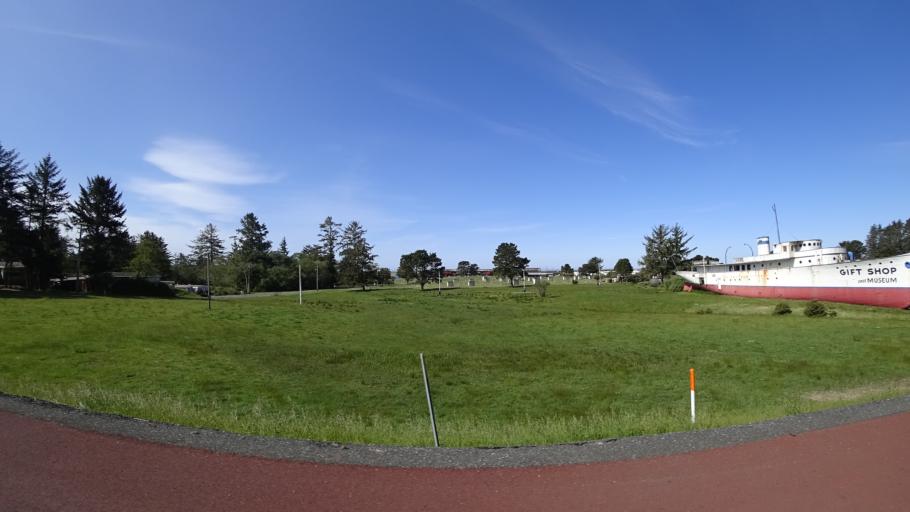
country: US
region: Oregon
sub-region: Curry County
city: Harbor
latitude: 41.9465
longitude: -124.1949
